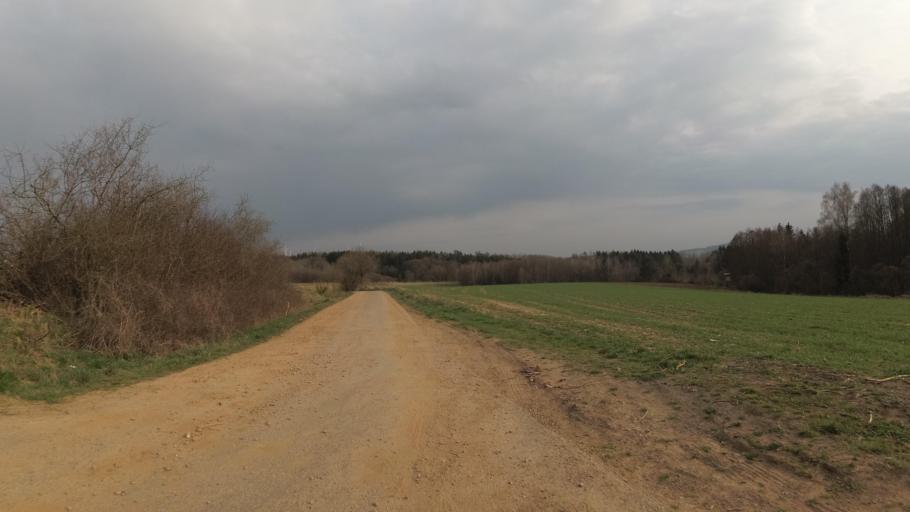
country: DE
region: Rheinland-Pfalz
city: Gimbweiler
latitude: 49.5852
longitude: 7.1736
